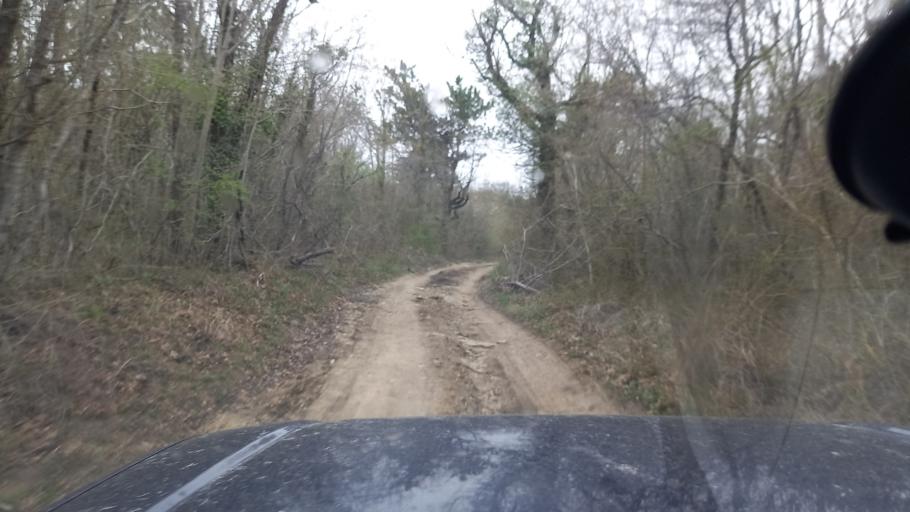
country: RU
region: Krasnodarskiy
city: Dzhubga
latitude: 44.3146
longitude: 38.6790
